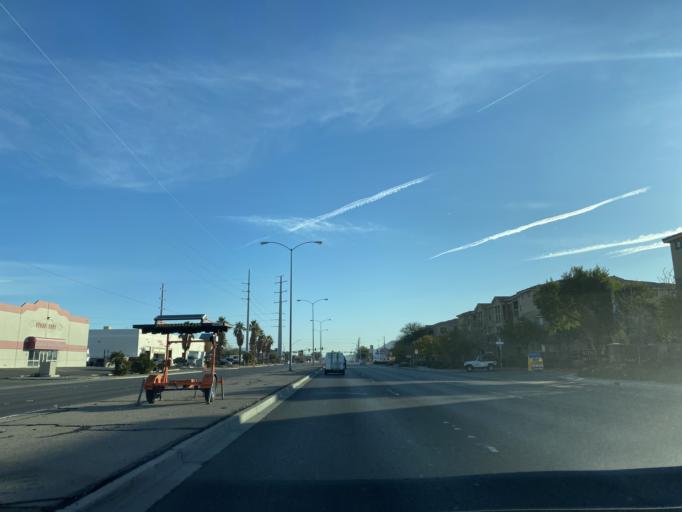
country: US
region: Nevada
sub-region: Clark County
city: Nellis Air Force Base
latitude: 36.2404
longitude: -115.0833
